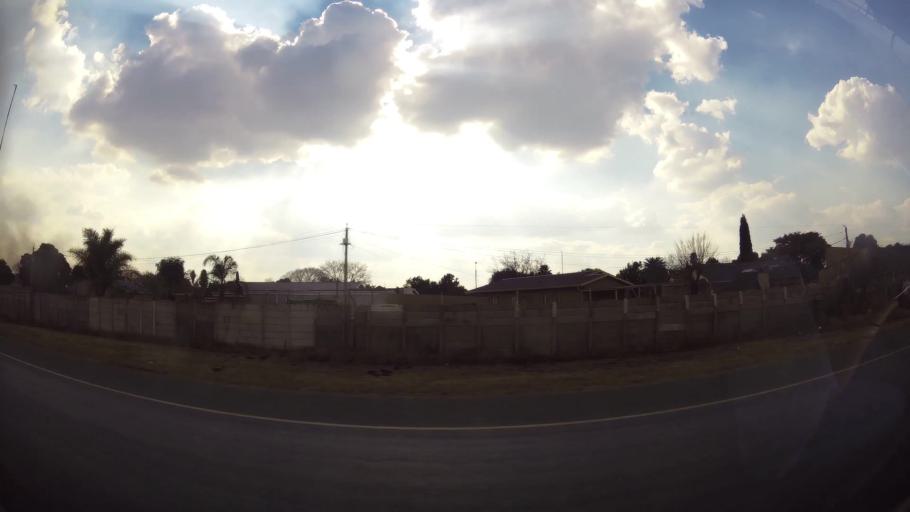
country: ZA
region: Gauteng
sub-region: Ekurhuleni Metropolitan Municipality
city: Boksburg
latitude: -26.2672
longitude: 28.2943
